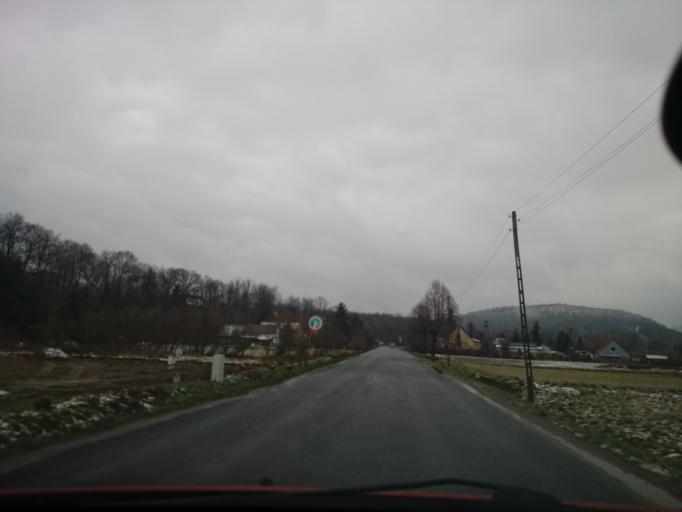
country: PL
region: Lower Silesian Voivodeship
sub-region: Powiat klodzki
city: Klodzko
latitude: 50.3885
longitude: 16.6268
